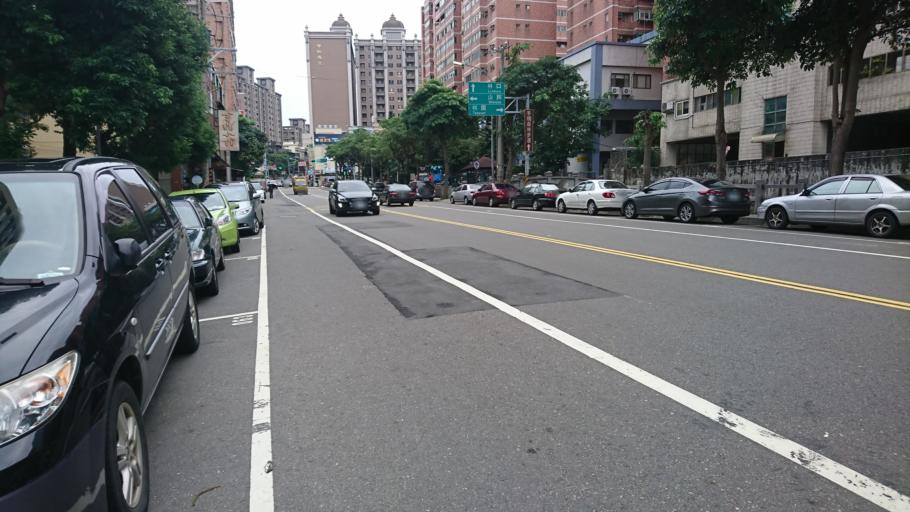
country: TW
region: Taiwan
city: Taoyuan City
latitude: 25.0527
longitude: 121.2988
